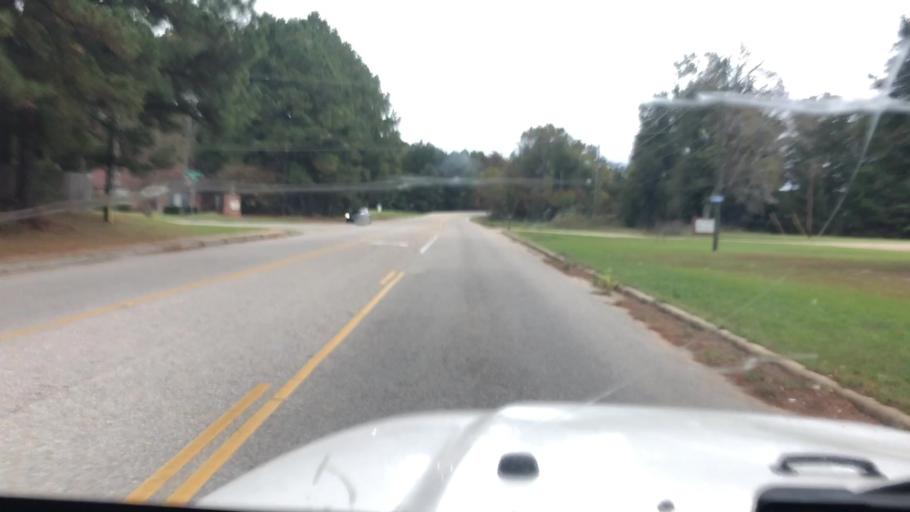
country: US
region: Alabama
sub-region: Elmore County
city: Blue Ridge
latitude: 32.4035
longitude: -86.1859
